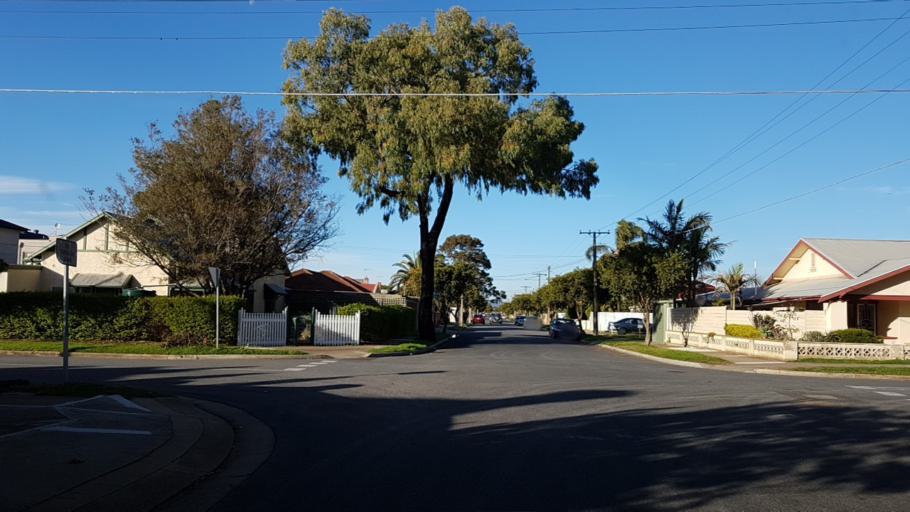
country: AU
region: South Australia
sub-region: Charles Sturt
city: Woodville North
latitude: -34.8678
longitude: 138.5436
